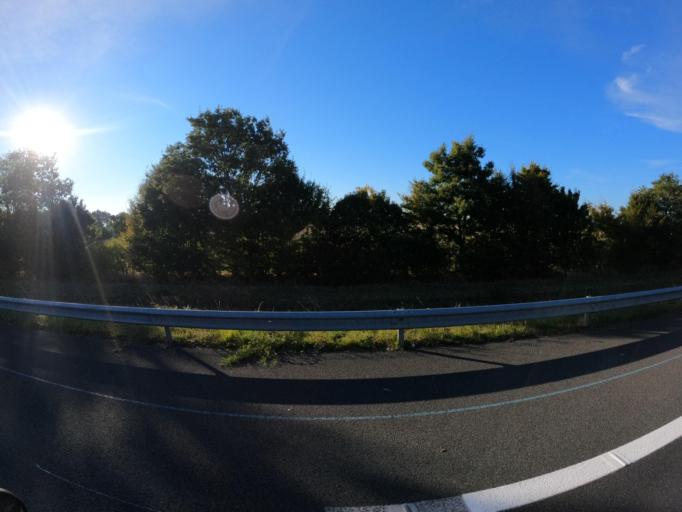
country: FR
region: Pays de la Loire
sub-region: Departement de Maine-et-Loire
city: Chemille-Melay
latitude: 47.2032
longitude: -0.7700
